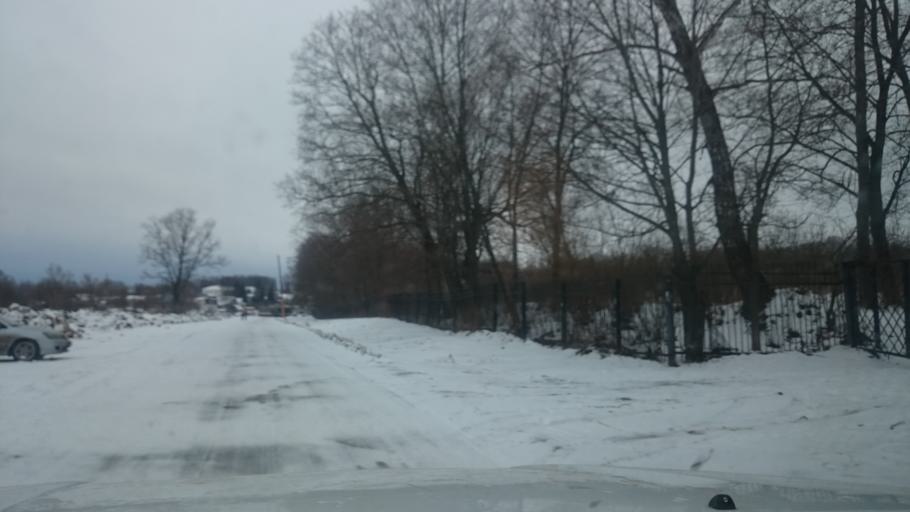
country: RU
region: Tula
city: Pervomayskiy
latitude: 54.0761
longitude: 37.5346
